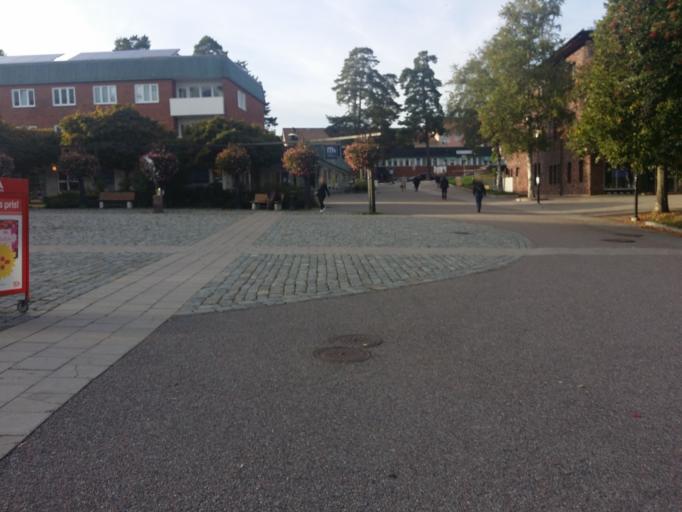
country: SE
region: Stockholm
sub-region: Upplands-Bro Kommun
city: Kungsaengen
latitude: 59.4791
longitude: 17.7510
